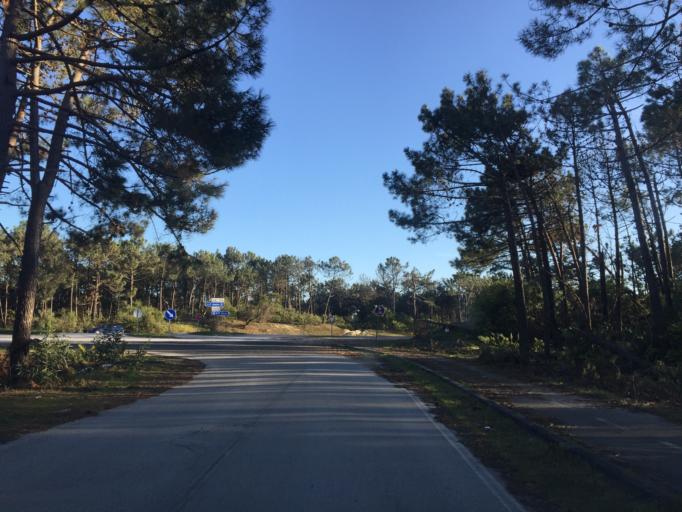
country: PT
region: Coimbra
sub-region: Figueira da Foz
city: Lavos
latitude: 40.0784
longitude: -8.8625
